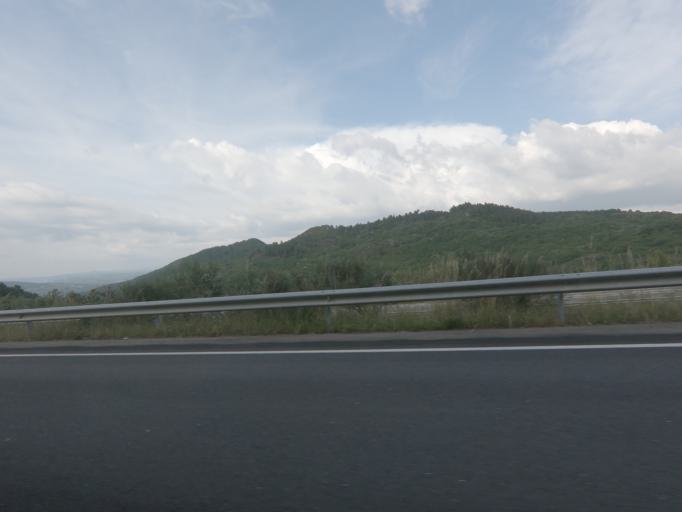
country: ES
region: Galicia
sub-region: Provincia de Ourense
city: Ambia
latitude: 42.1710
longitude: -7.7625
